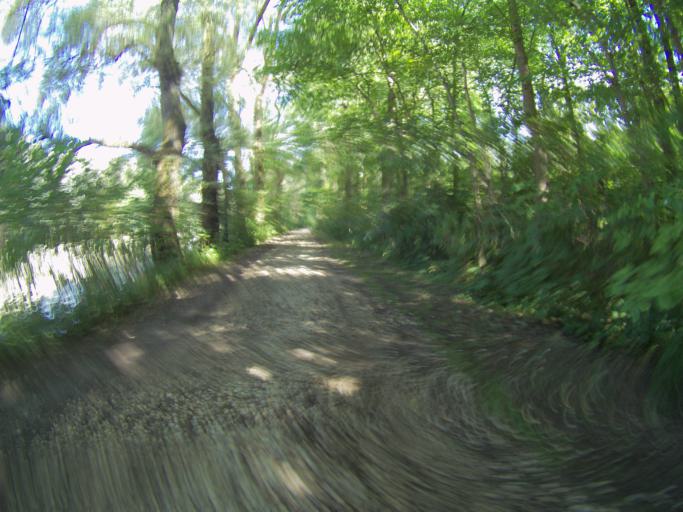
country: DE
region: Bavaria
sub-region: Upper Bavaria
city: Marzling
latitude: 48.4052
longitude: 11.8050
